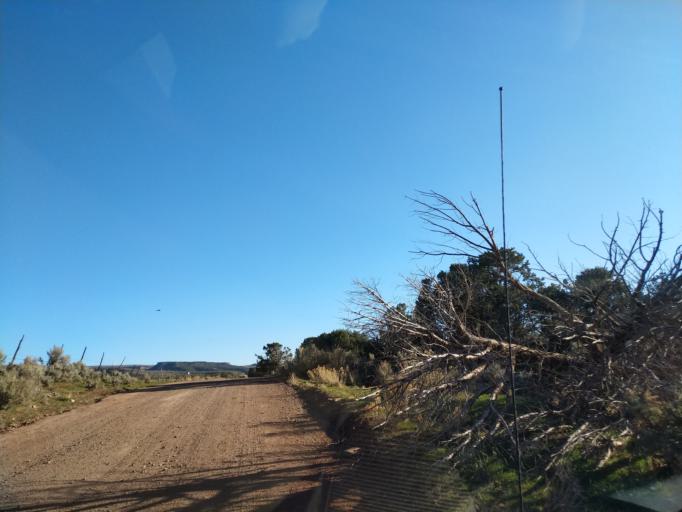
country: US
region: Colorado
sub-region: Mesa County
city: Loma
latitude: 38.9517
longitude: -109.0533
